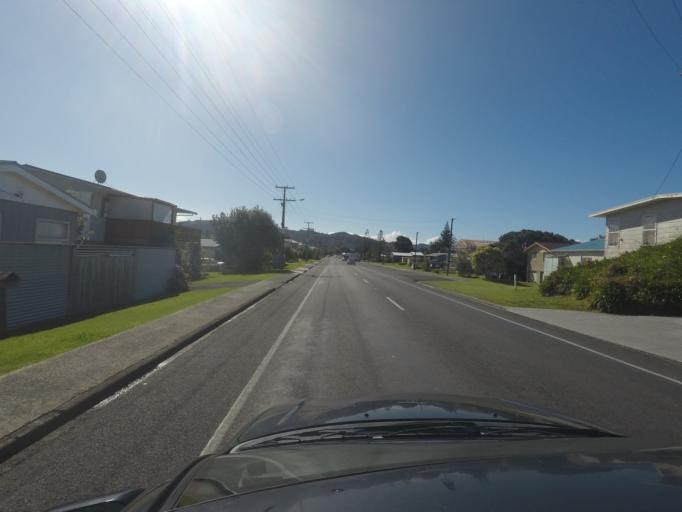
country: NZ
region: Bay of Plenty
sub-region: Western Bay of Plenty District
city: Waihi Beach
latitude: -37.4147
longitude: 175.9473
